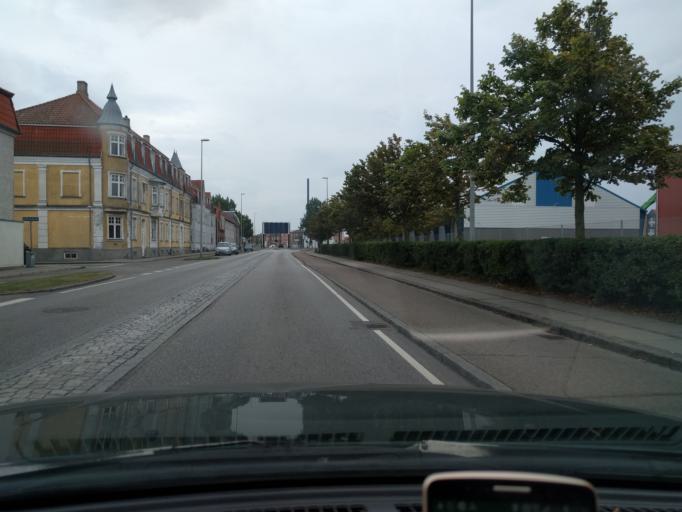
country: DK
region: Zealand
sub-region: Slagelse Kommune
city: Korsor
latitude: 55.3335
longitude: 11.1413
